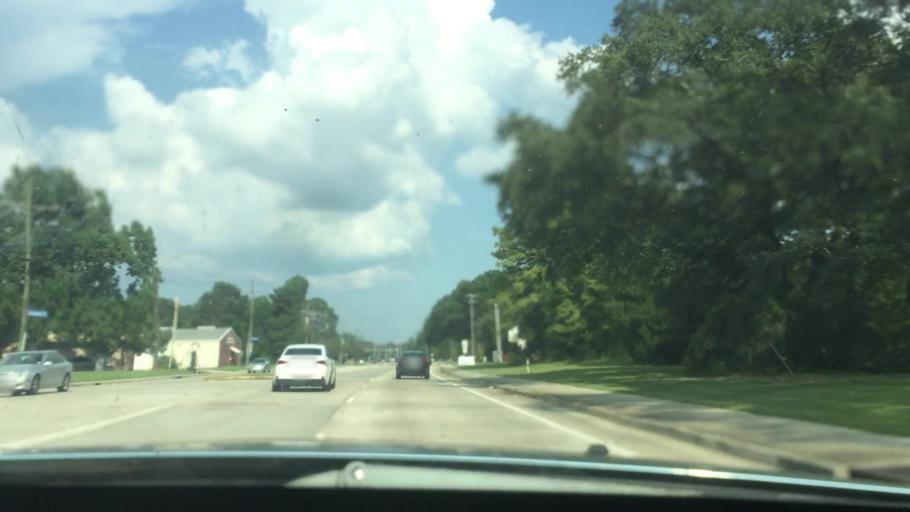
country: US
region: Louisiana
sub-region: East Baton Rouge Parish
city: Shenandoah
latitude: 30.4282
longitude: -91.0190
